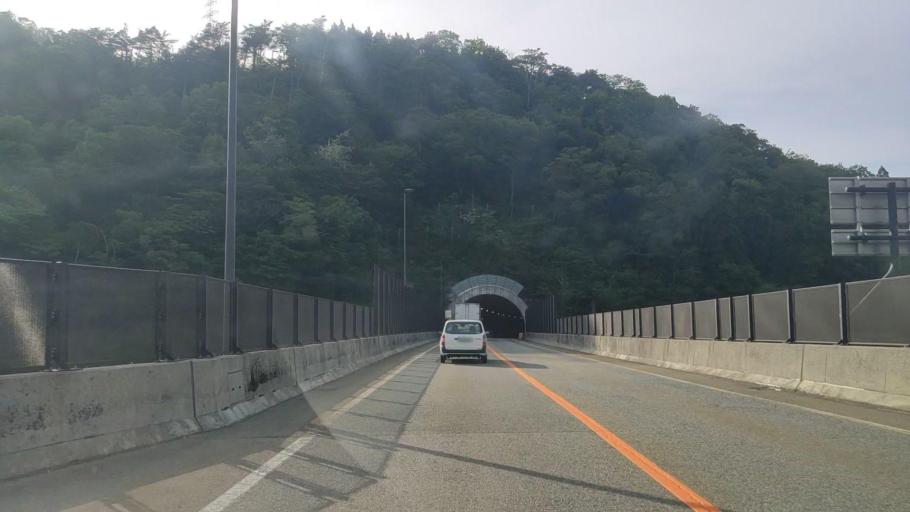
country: JP
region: Toyama
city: Yatsuomachi-higashikumisaka
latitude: 36.5271
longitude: 137.2287
